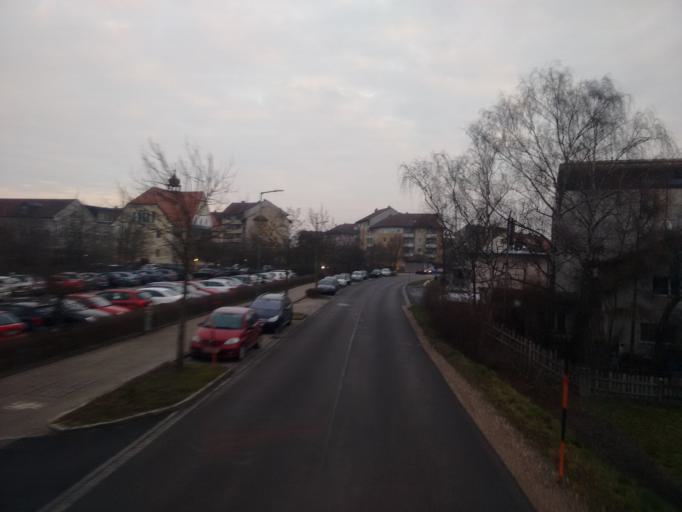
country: AT
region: Upper Austria
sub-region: Wels Stadt
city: Wels
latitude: 48.1714
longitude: 14.0152
